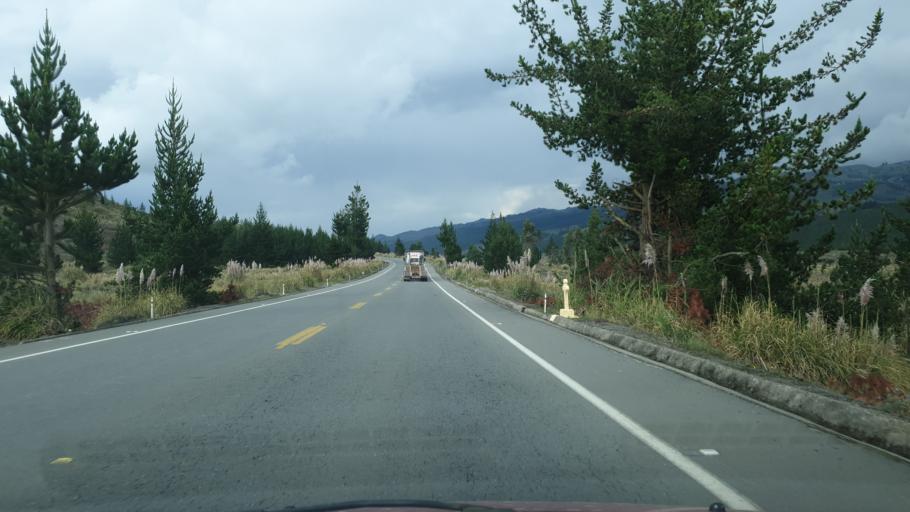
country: EC
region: Chimborazo
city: Alausi
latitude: -2.0465
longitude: -78.7407
